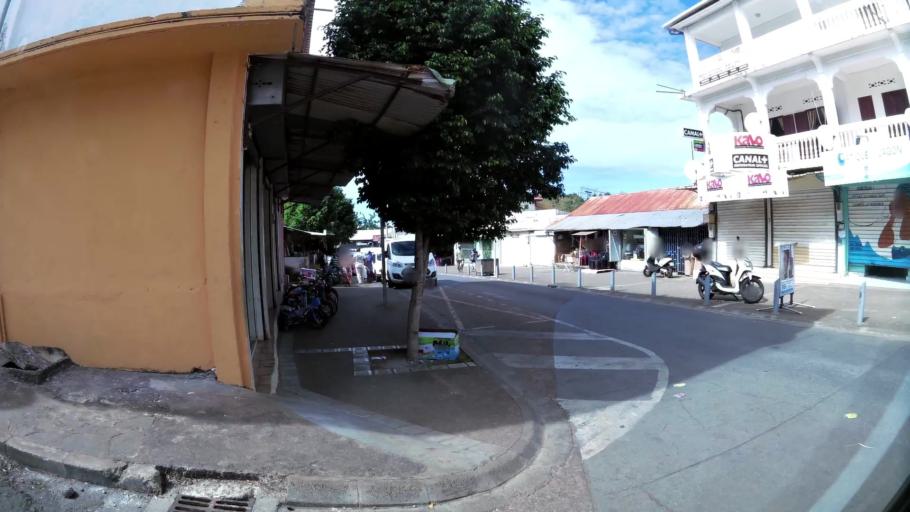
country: YT
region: Mamoudzou
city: Mamoudzou
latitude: -12.7819
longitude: 45.2311
